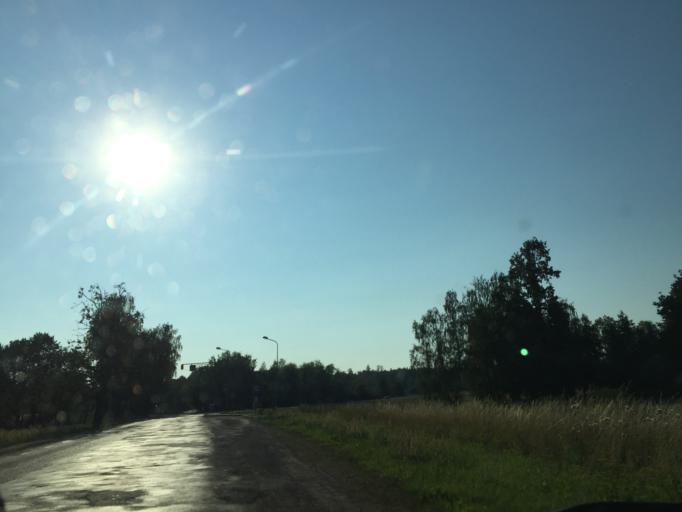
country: LV
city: Tervete
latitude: 56.4221
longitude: 23.5495
